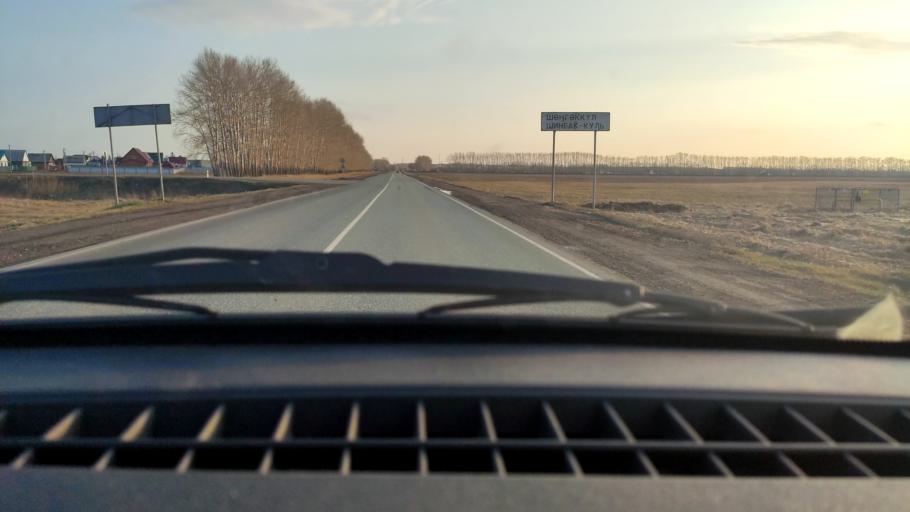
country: RU
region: Bashkortostan
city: Chishmy
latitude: 54.3994
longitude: 55.2112
